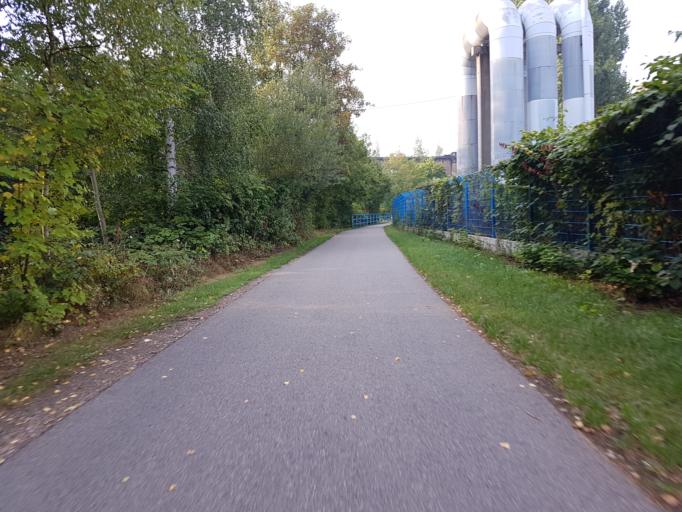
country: DE
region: Saxony
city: Chemnitz
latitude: 50.8551
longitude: 12.9263
